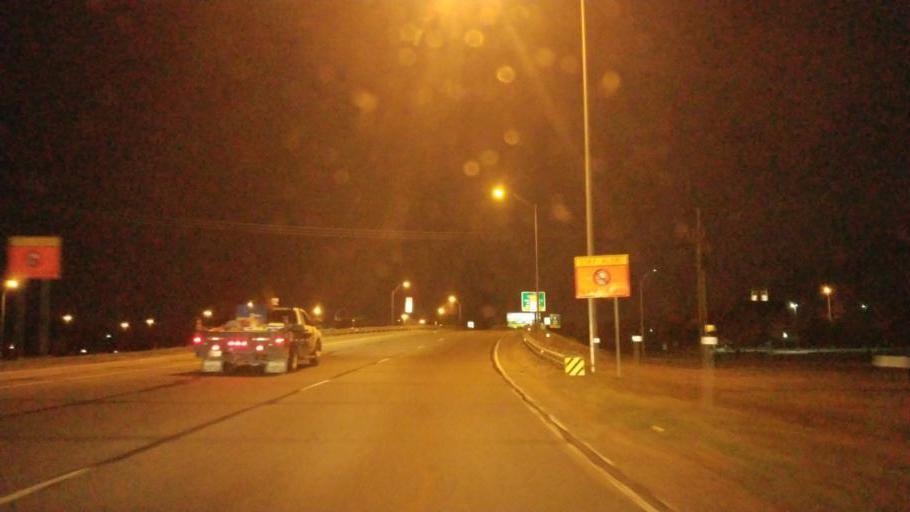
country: US
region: Texas
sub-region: Potter County
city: Amarillo
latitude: 35.2015
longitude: -101.8346
